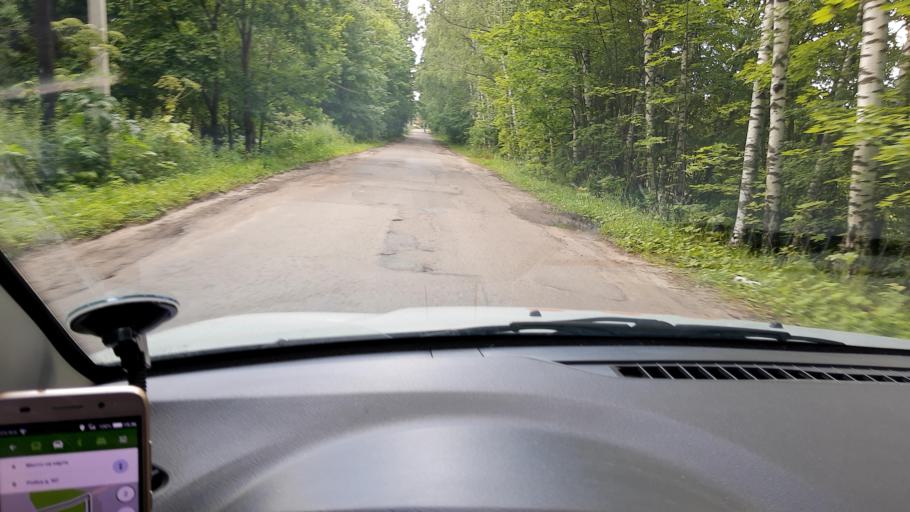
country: RU
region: Nizjnij Novgorod
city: Afonino
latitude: 56.2021
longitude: 44.0249
